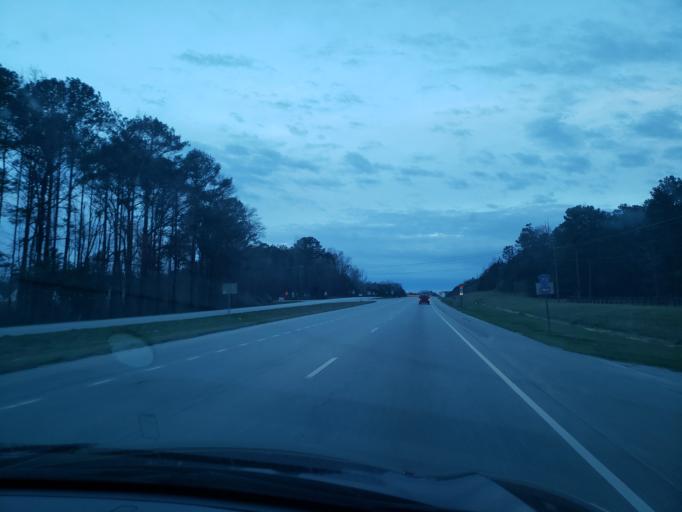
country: US
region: Alabama
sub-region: Lee County
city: Auburn
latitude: 32.6640
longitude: -85.4716
